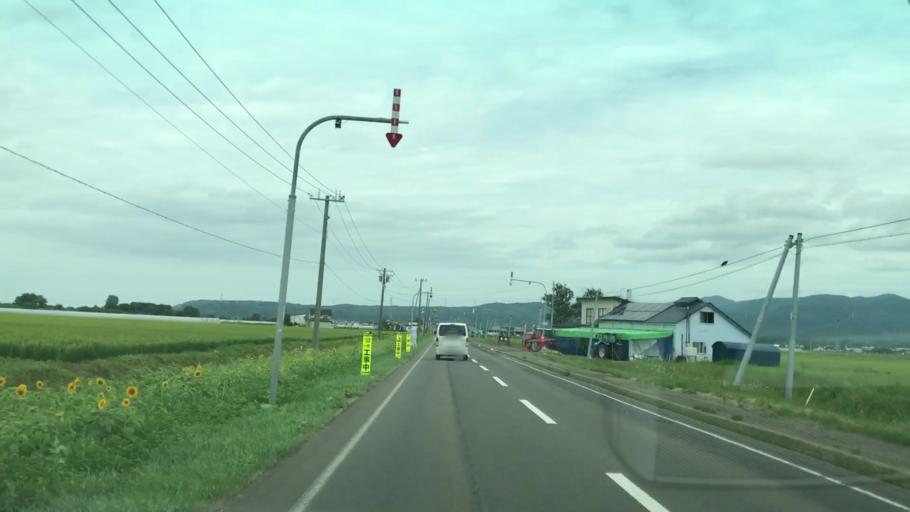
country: JP
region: Hokkaido
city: Iwanai
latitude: 43.0065
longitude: 140.5813
